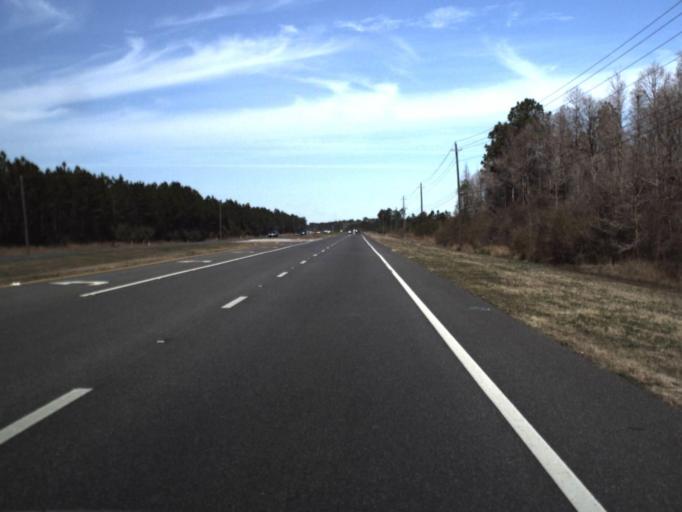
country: US
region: Florida
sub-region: Bay County
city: Lynn Haven
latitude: 30.3437
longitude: -85.6616
